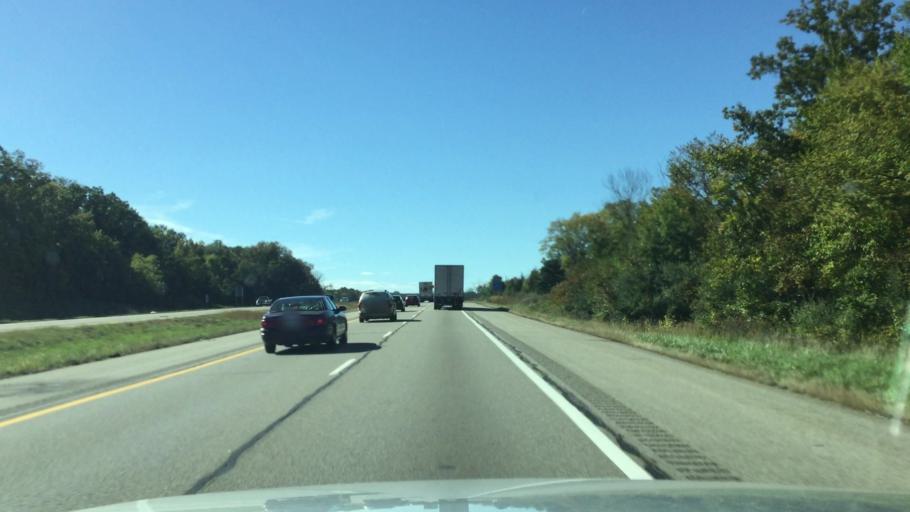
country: US
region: Michigan
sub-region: Washtenaw County
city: Ypsilanti
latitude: 42.3258
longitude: -83.6558
